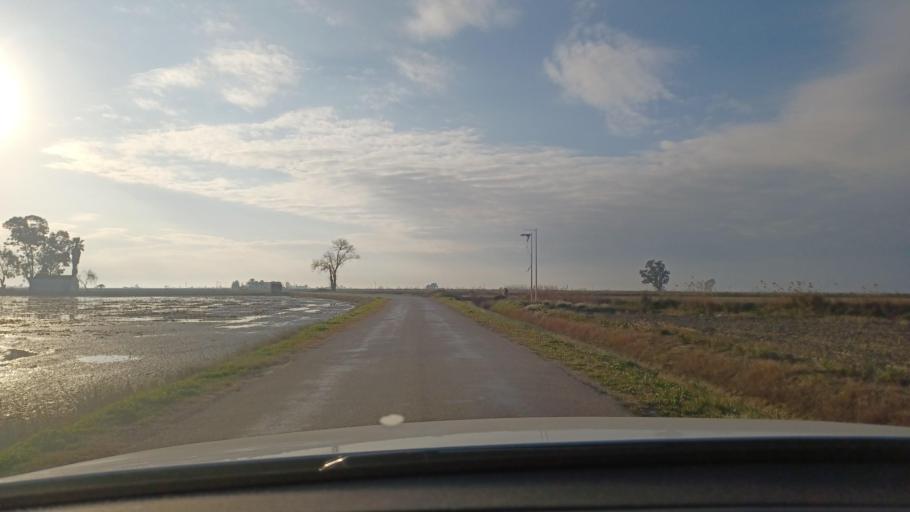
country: ES
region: Catalonia
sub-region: Provincia de Tarragona
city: Deltebre
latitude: 40.6889
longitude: 0.6519
